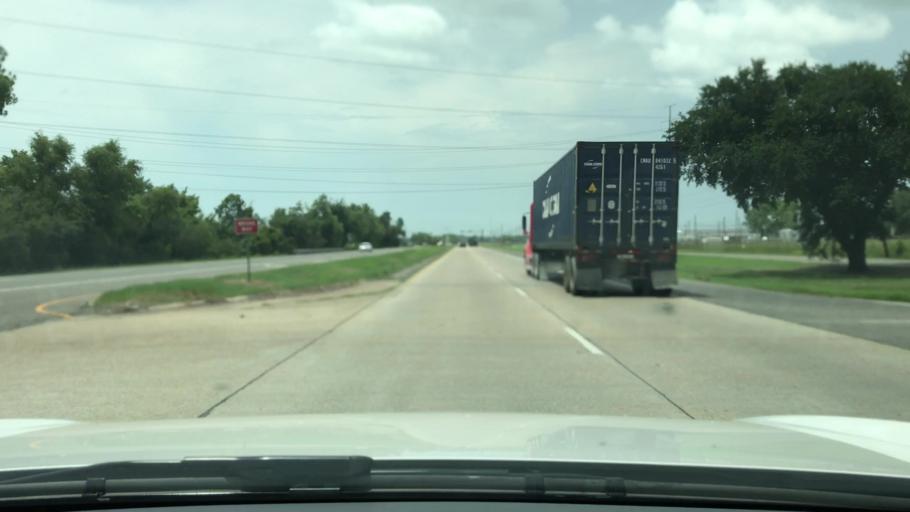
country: US
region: Louisiana
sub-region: West Baton Rouge Parish
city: Addis
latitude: 30.3295
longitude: -91.2556
